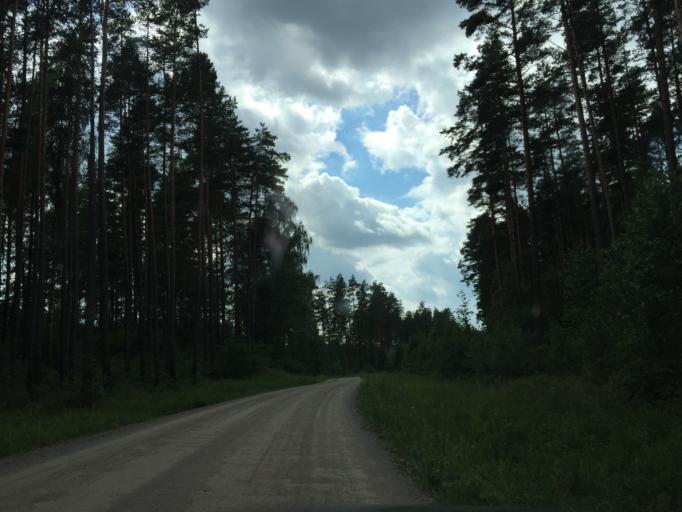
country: LV
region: Jelgava
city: Jelgava
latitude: 56.6262
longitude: 23.6503
